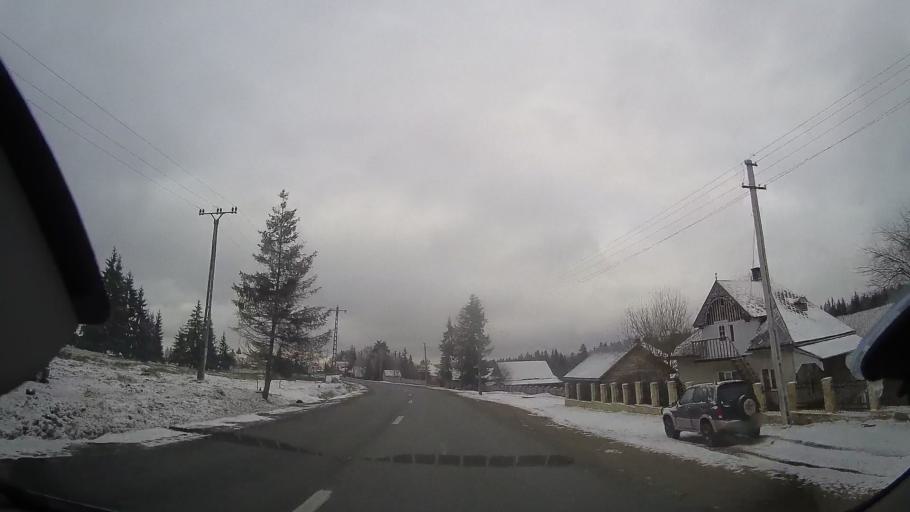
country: RO
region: Cluj
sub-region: Comuna Belis
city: Belis
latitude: 46.7027
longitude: 23.0370
